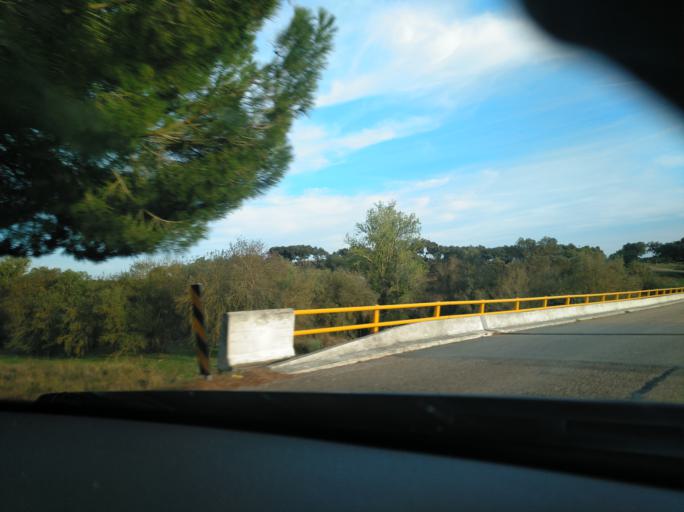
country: PT
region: Portalegre
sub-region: Avis
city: Avis
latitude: 38.8767
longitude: -7.8271
